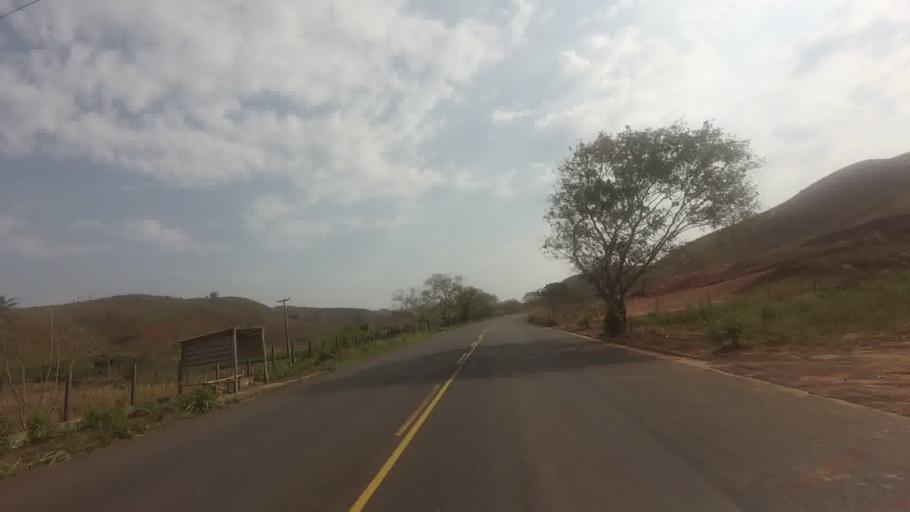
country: BR
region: Rio de Janeiro
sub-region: Itaperuna
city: Itaperuna
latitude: -21.2805
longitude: -41.7904
